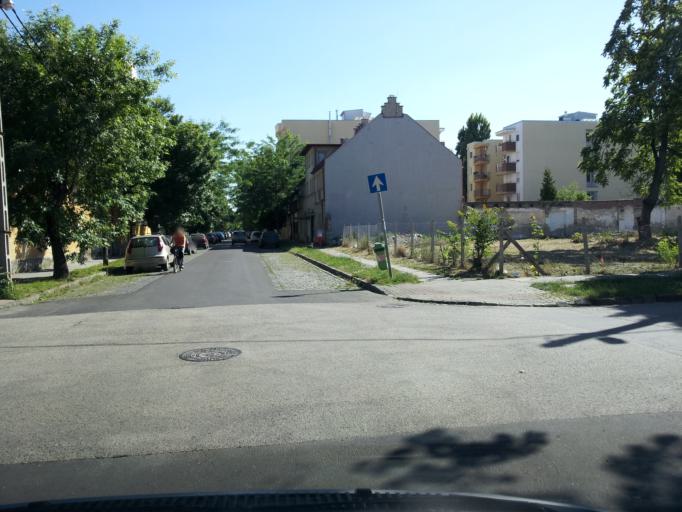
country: HU
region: Budapest
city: Budapest XIII. keruelet
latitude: 47.5348
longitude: 19.0857
